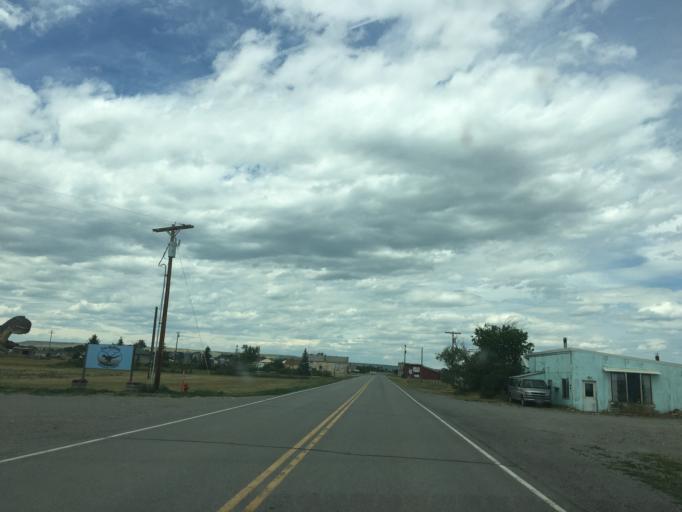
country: US
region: Montana
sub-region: Teton County
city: Choteau
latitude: 47.9760
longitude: -112.3109
